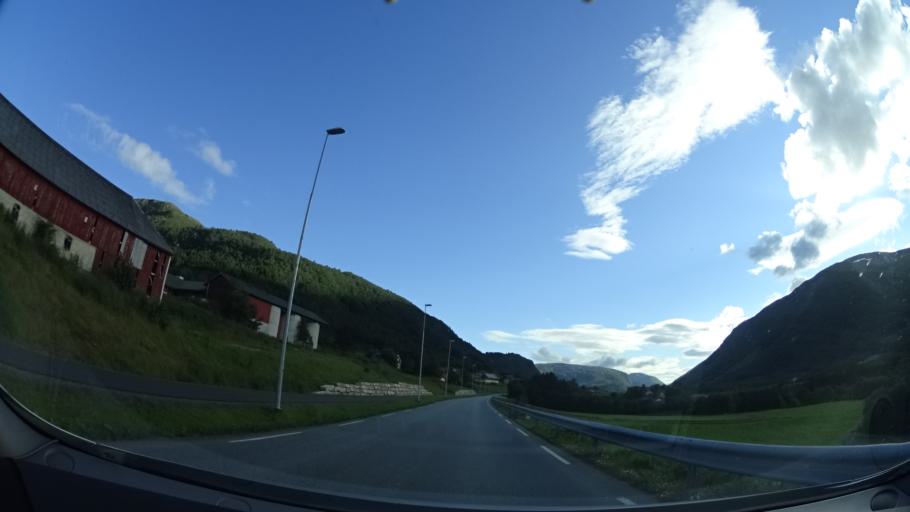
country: NO
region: More og Romsdal
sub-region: Gjemnes
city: Batnfjordsora
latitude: 62.8775
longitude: 7.6489
